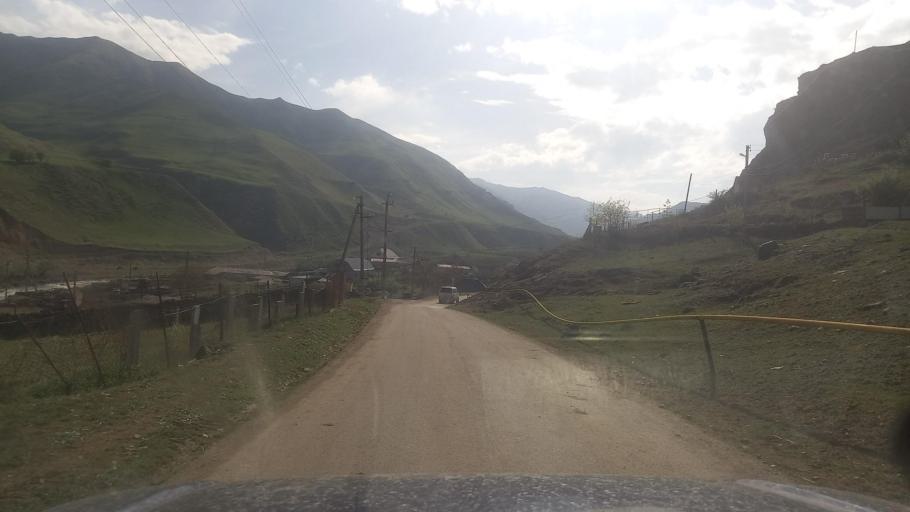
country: RU
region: Kabardino-Balkariya
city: Kamennomostskoye
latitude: 43.7257
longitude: 42.9222
